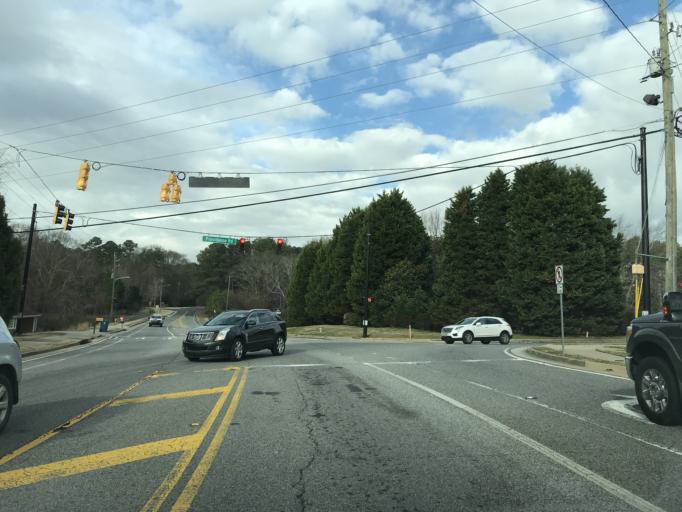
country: US
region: Georgia
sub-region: Fulton County
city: Alpharetta
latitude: 34.0876
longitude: -84.3077
